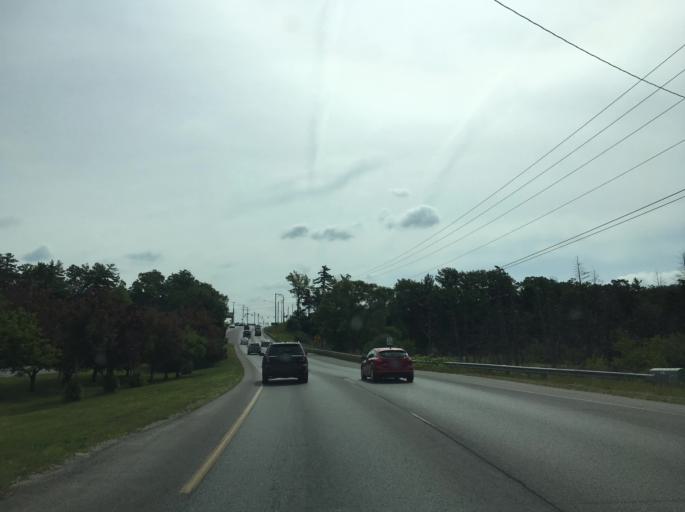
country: US
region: Michigan
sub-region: Grand Traverse County
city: Traverse City
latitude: 44.7333
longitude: -85.6151
